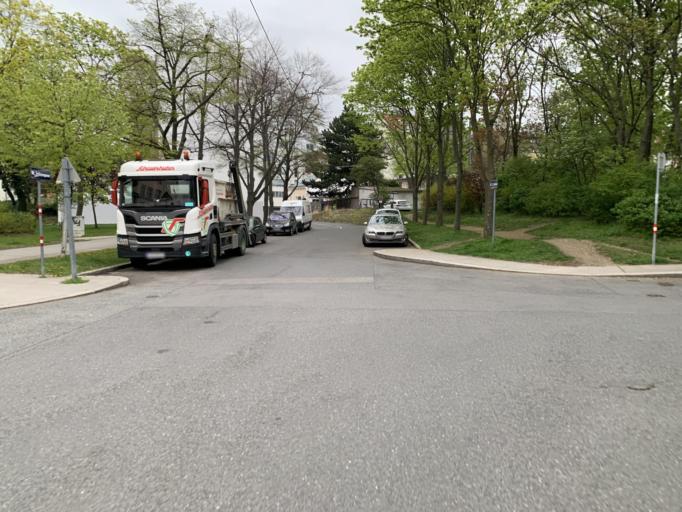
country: AT
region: Vienna
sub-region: Wien Stadt
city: Vienna
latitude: 48.1662
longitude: 16.3791
